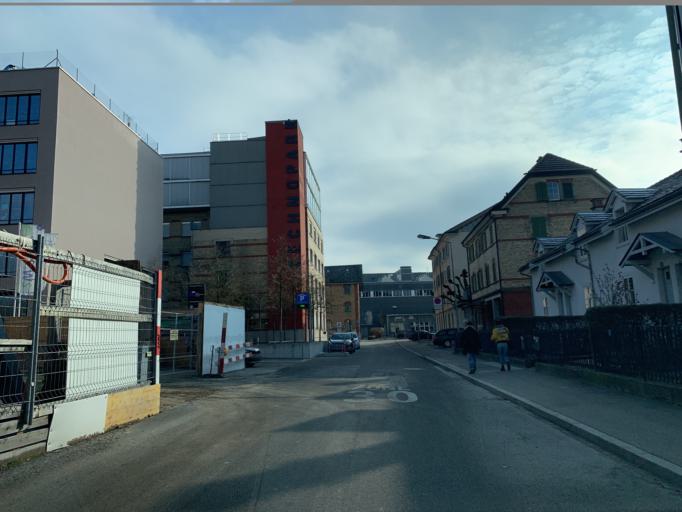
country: CH
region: Zurich
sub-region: Bezirk Winterthur
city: Stadt Winterthur (Kreis 1) / Toessfeld
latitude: 47.4946
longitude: 8.7155
